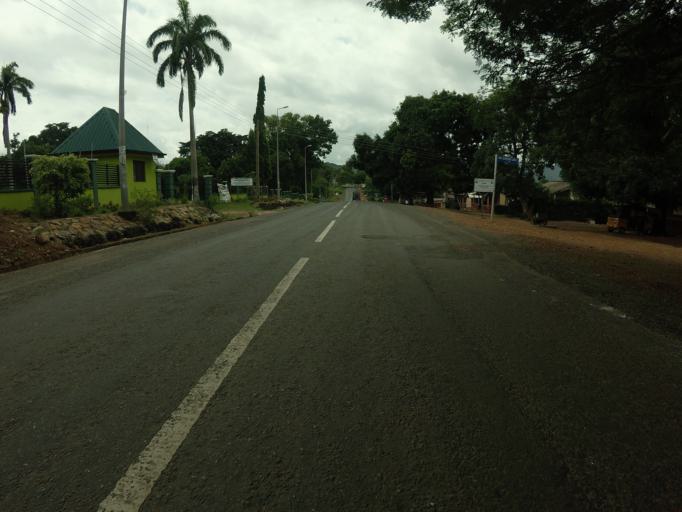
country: GH
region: Volta
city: Ho
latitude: 6.6054
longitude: 0.4658
